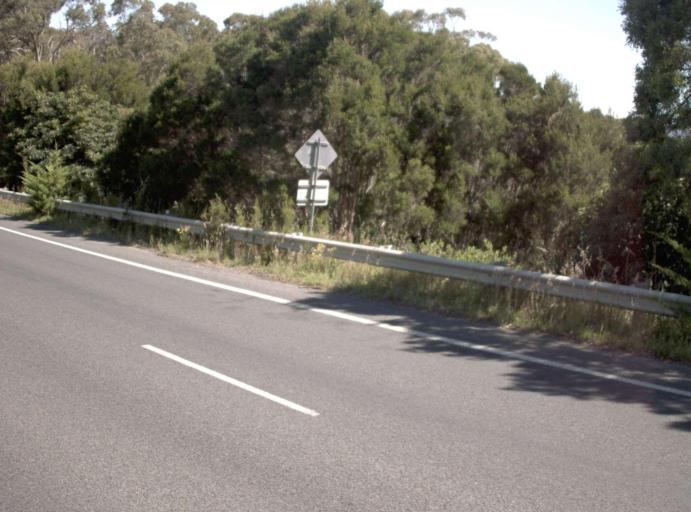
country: AU
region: Victoria
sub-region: Latrobe
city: Morwell
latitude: -38.6428
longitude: 146.2031
